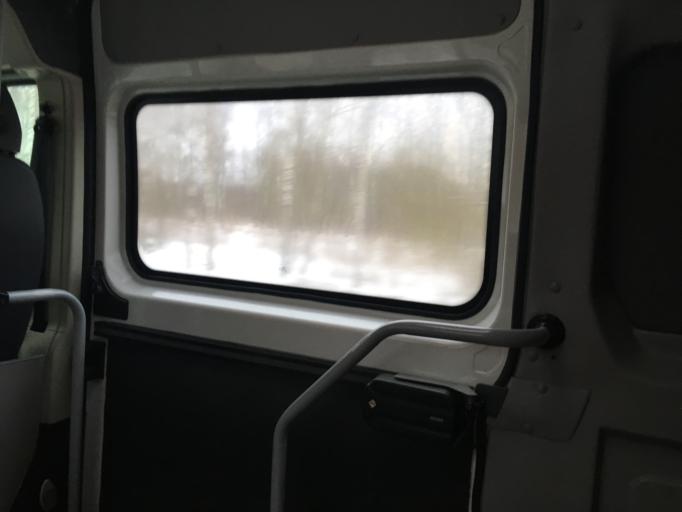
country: RU
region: Tula
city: Pervomayskiy
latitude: 54.1314
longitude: 37.3268
